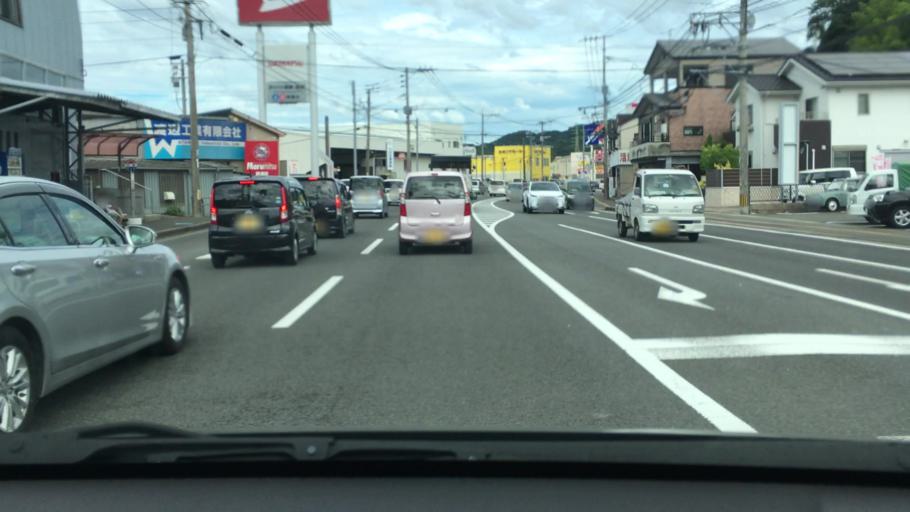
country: JP
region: Nagasaki
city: Togitsu
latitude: 32.8339
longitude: 129.8424
